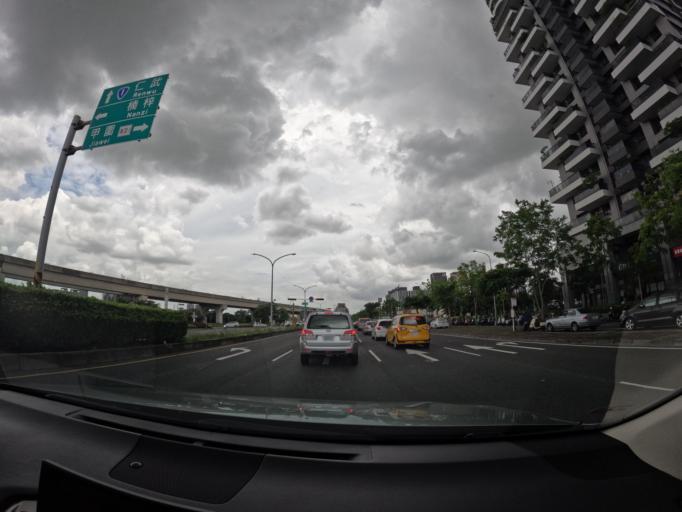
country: TW
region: Taiwan
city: Fengshan
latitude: 22.7439
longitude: 120.3167
